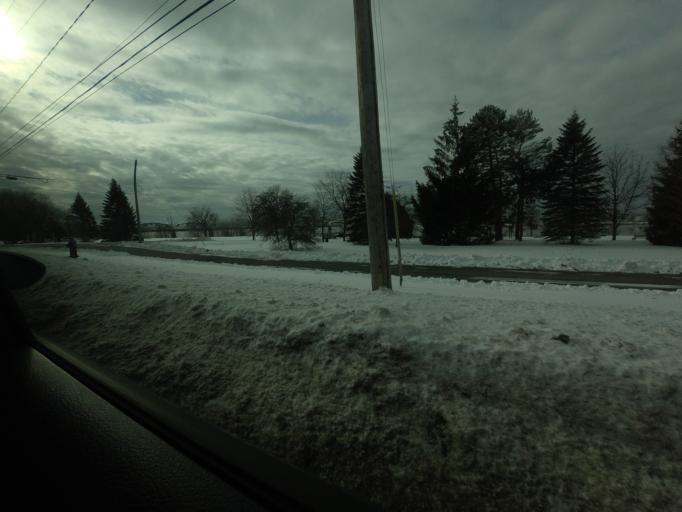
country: CA
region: New Brunswick
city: Fredericton
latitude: 45.9622
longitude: -66.6254
